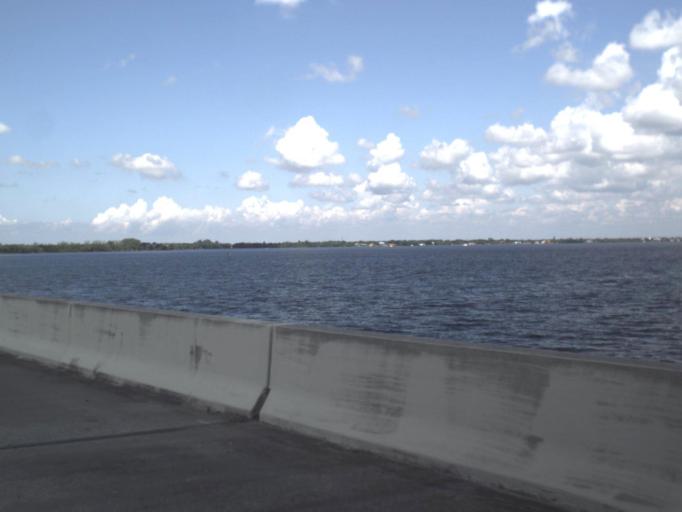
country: US
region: Florida
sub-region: Lee County
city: Whiskey Creek
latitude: 26.6051
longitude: -81.9066
